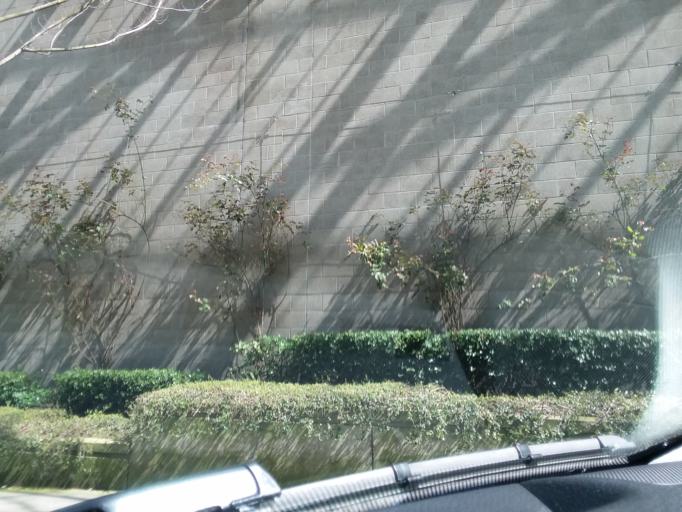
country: US
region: Washington
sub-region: King County
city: Seattle
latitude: 47.6160
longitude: -122.3371
